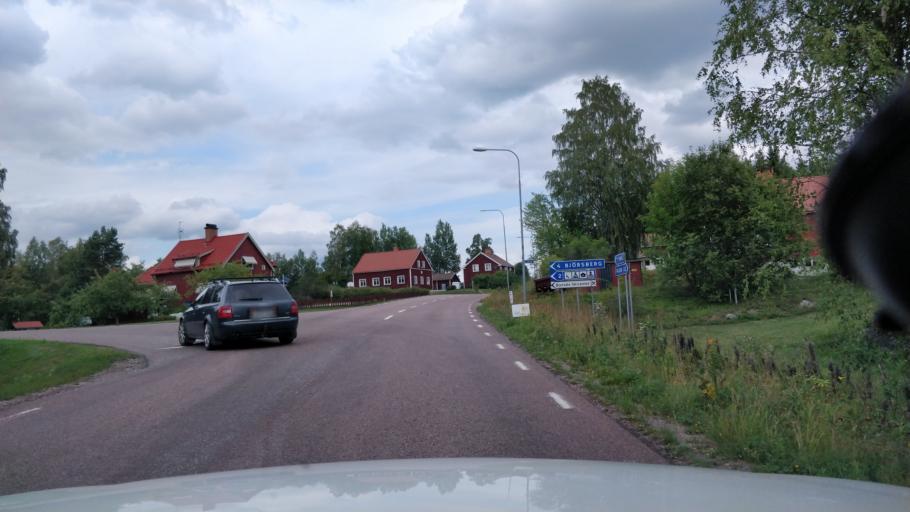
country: SE
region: Dalarna
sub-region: Faluns Kommun
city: Bjursas
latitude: 60.7450
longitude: 15.4693
